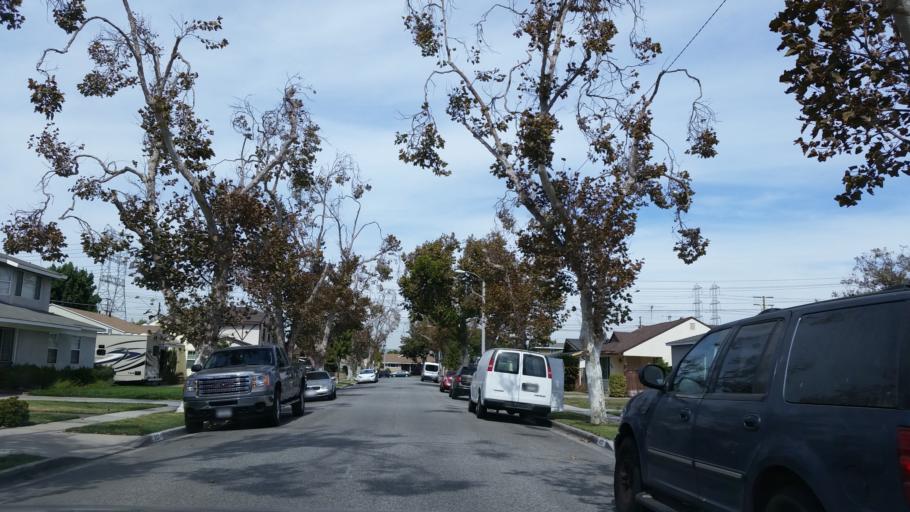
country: US
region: California
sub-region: Los Angeles County
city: Lakewood
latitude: 33.8664
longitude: -118.1281
